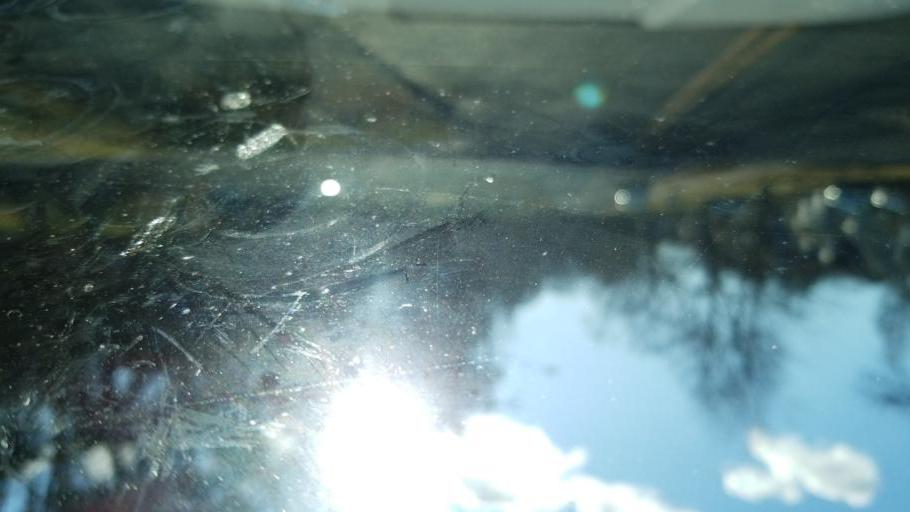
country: US
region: Connecticut
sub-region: Middlesex County
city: Middletown
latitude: 41.5430
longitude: -72.6604
